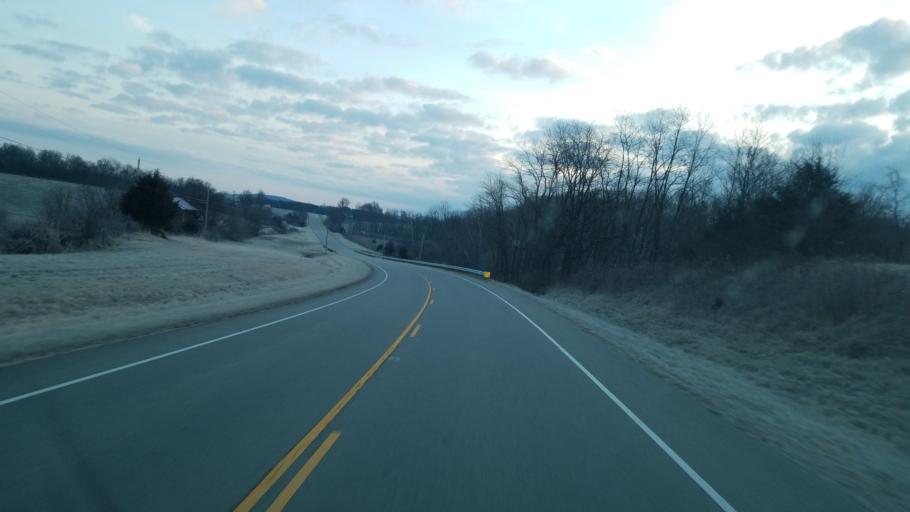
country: US
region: Ohio
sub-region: Highland County
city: Greenfield
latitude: 39.2219
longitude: -83.4020
